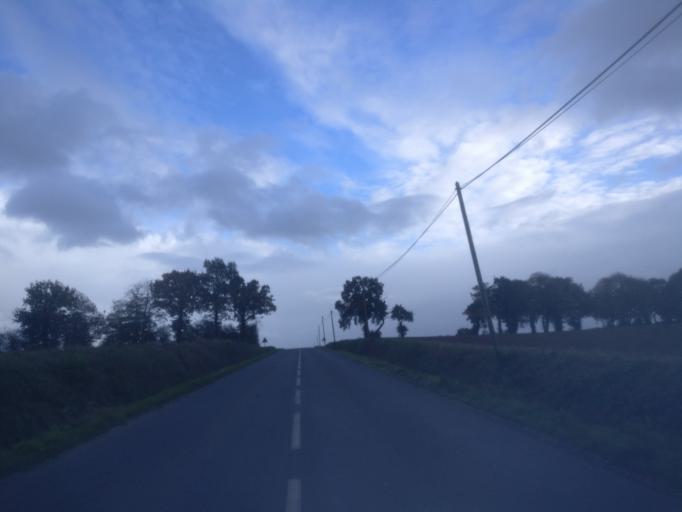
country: FR
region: Brittany
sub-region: Departement d'Ille-et-Vilaine
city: Breal-sous-Montfort
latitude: 48.0426
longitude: -1.8448
